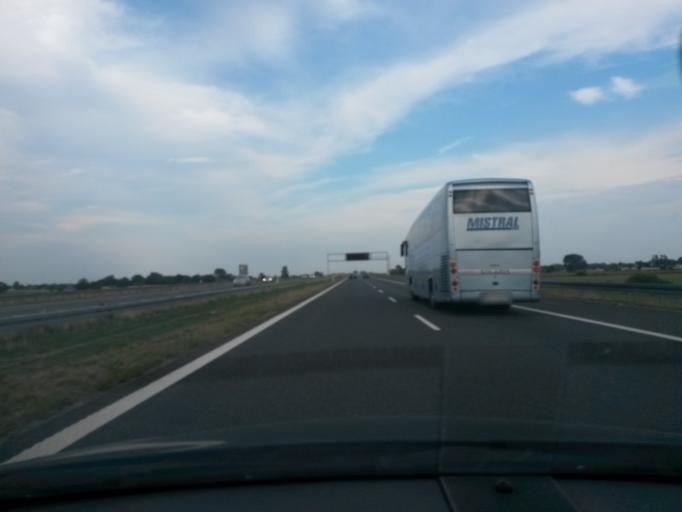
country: PL
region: Lodz Voivodeship
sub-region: Powiat poddebicki
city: Wartkowice
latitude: 51.9984
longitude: 19.0149
